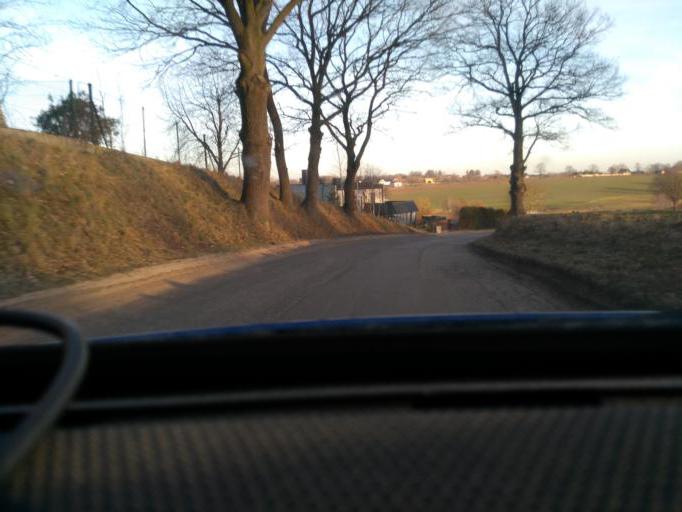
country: PL
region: Pomeranian Voivodeship
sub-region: Powiat kartuski
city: Przodkowo
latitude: 54.4101
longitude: 18.3258
